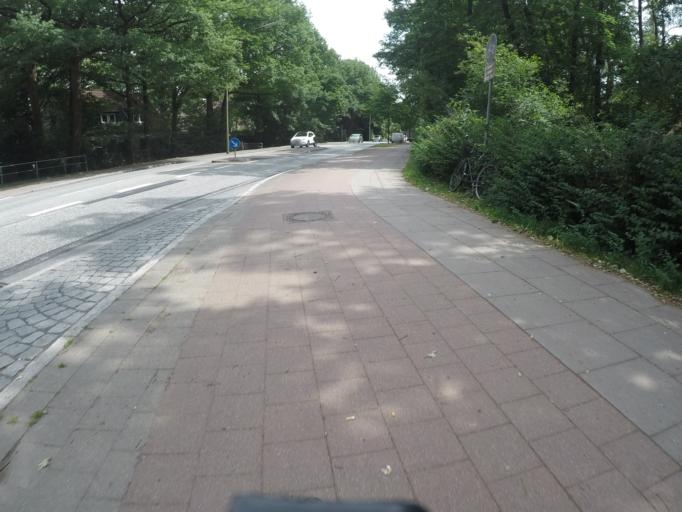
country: DE
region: Hamburg
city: Langenhorn
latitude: 53.6490
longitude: 9.9921
